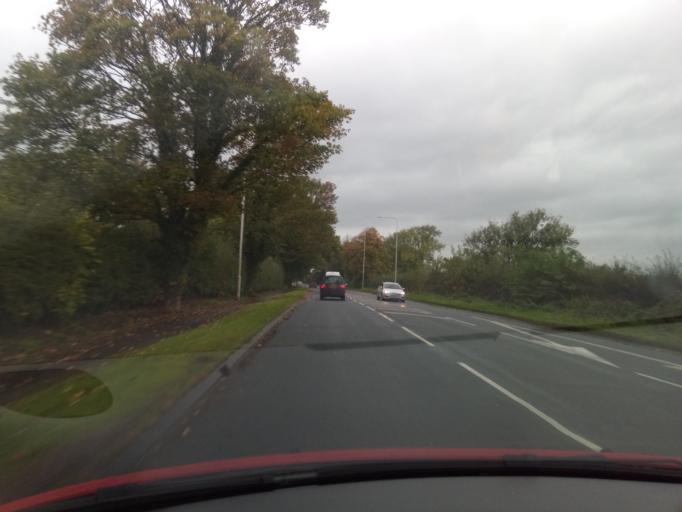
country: GB
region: England
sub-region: Lancashire
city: Catterall
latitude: 53.8452
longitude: -2.7433
